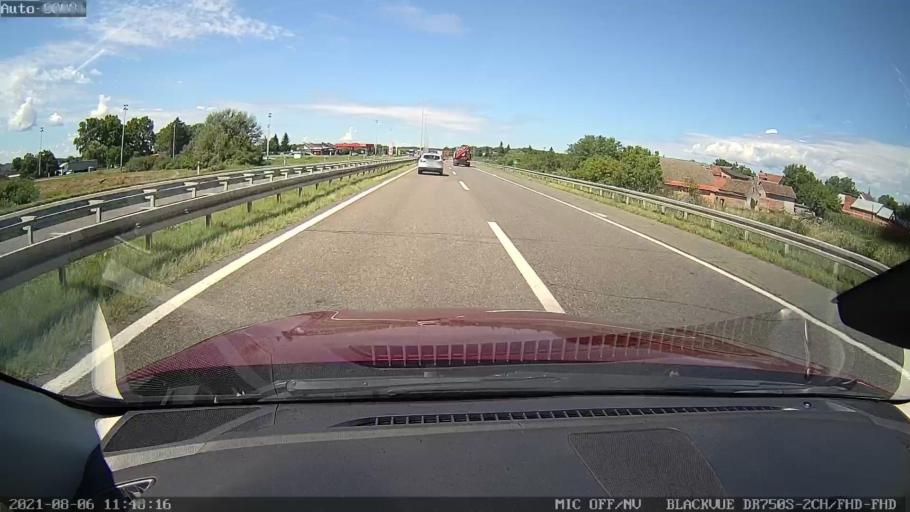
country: HR
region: Brodsko-Posavska
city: Luzani
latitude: 45.1626
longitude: 17.7045
